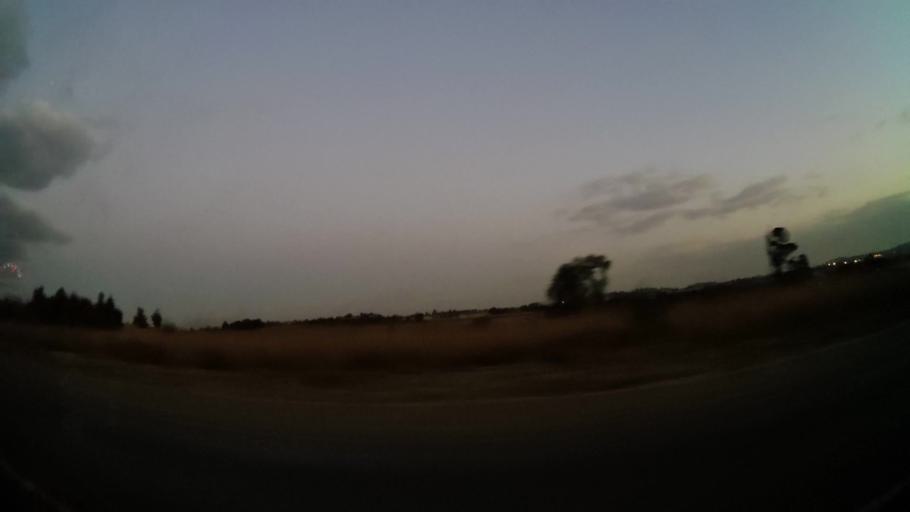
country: ZA
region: Gauteng
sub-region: West Rand District Municipality
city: Krugersdorp
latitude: -26.1033
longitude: 27.7350
